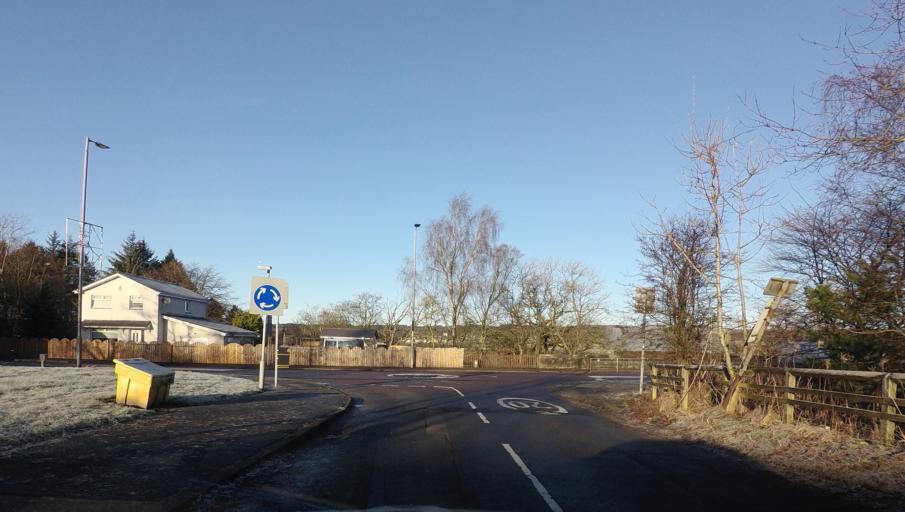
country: GB
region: Scotland
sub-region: North Lanarkshire
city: Shotts
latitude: 55.8020
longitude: -3.8250
